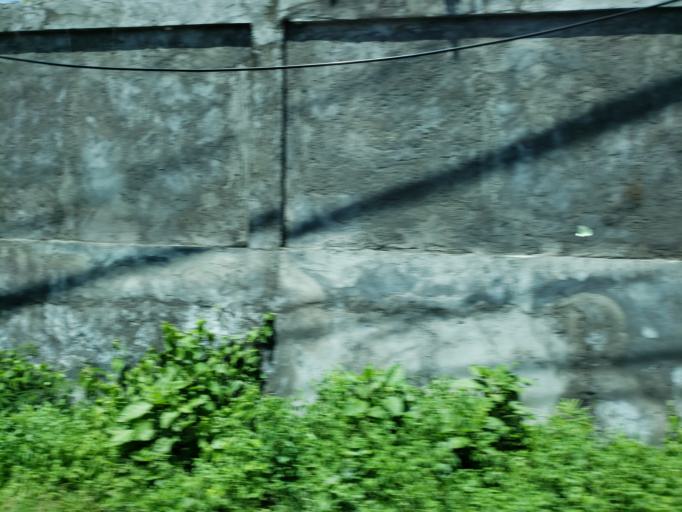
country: ID
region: Bali
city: Kangin
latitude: -8.8300
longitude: 115.1361
